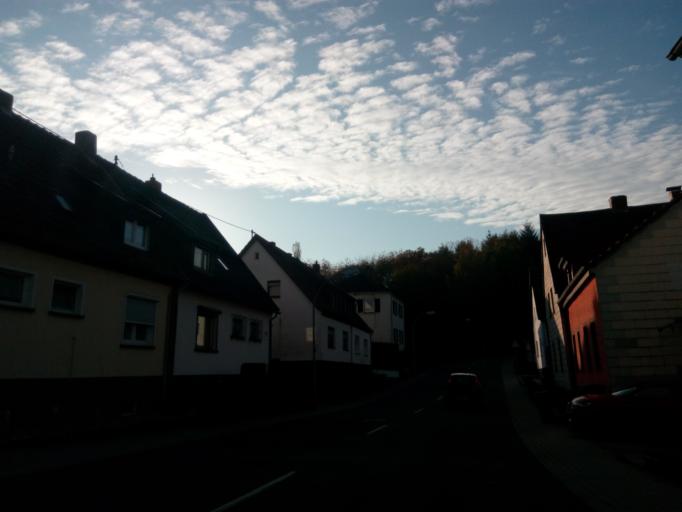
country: DE
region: Saarland
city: Sulzbach
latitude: 49.2813
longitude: 7.0230
